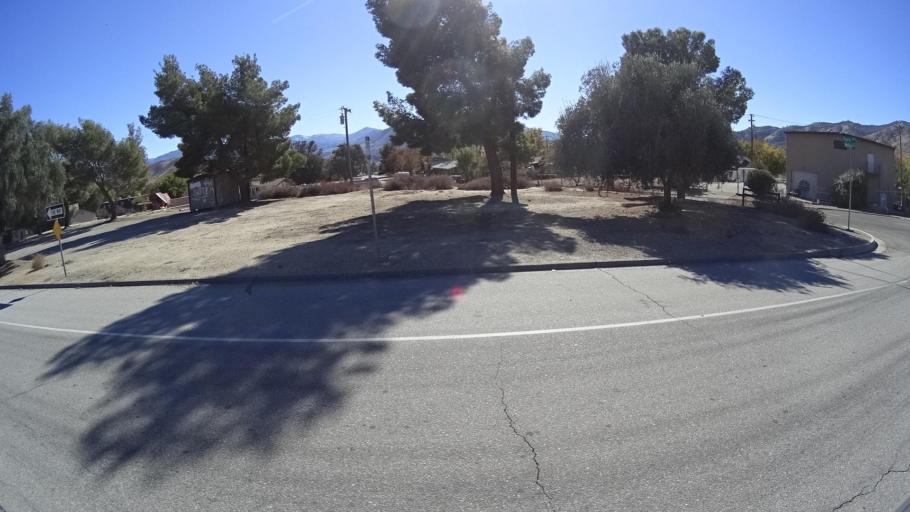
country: US
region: California
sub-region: Kern County
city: Wofford Heights
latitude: 35.7083
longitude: -118.4527
